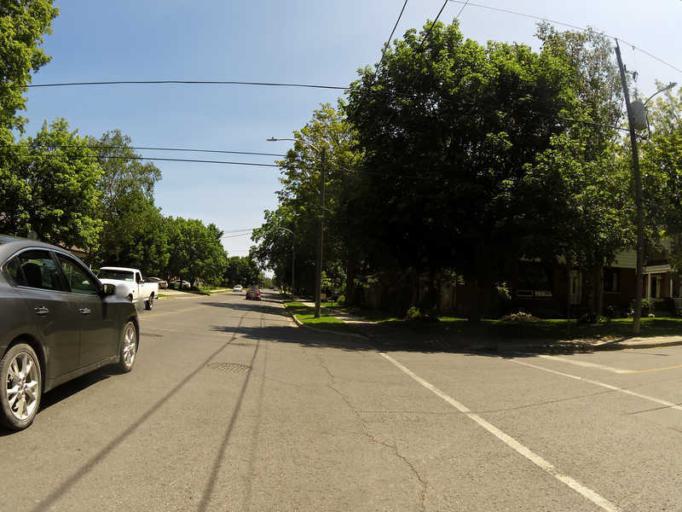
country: CA
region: Ontario
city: Peterborough
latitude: 44.2925
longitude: -78.3170
